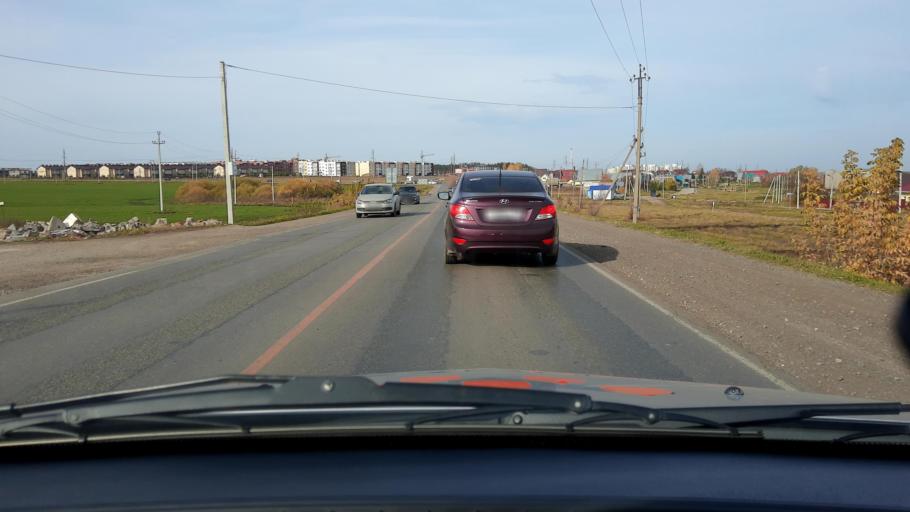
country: RU
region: Bashkortostan
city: Avdon
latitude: 54.7399
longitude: 55.8008
